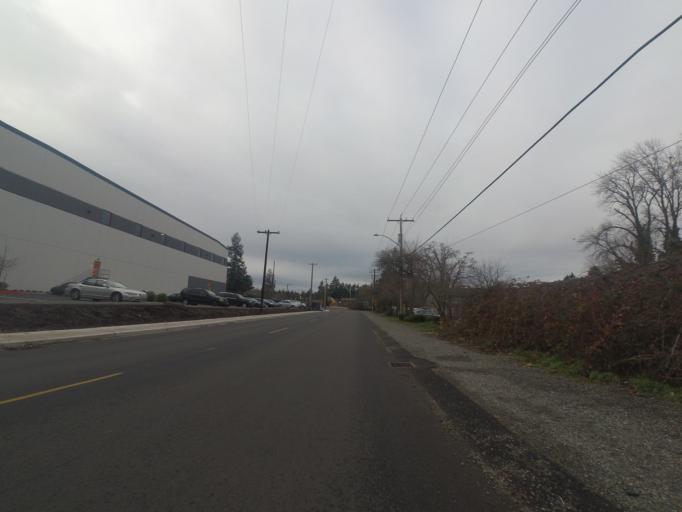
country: US
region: Washington
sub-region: Pierce County
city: Fort Lewis
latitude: 47.1249
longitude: -122.5355
